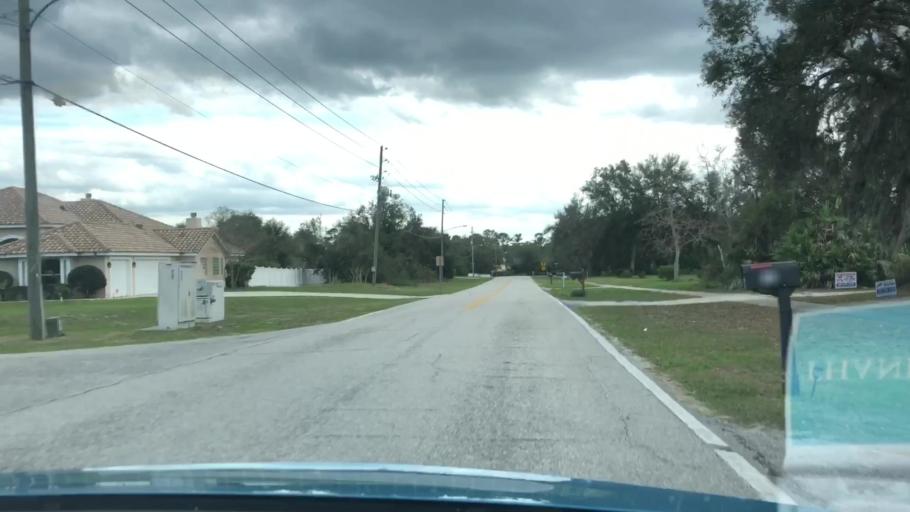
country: US
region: Florida
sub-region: Volusia County
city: Deltona
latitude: 28.8774
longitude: -81.2206
